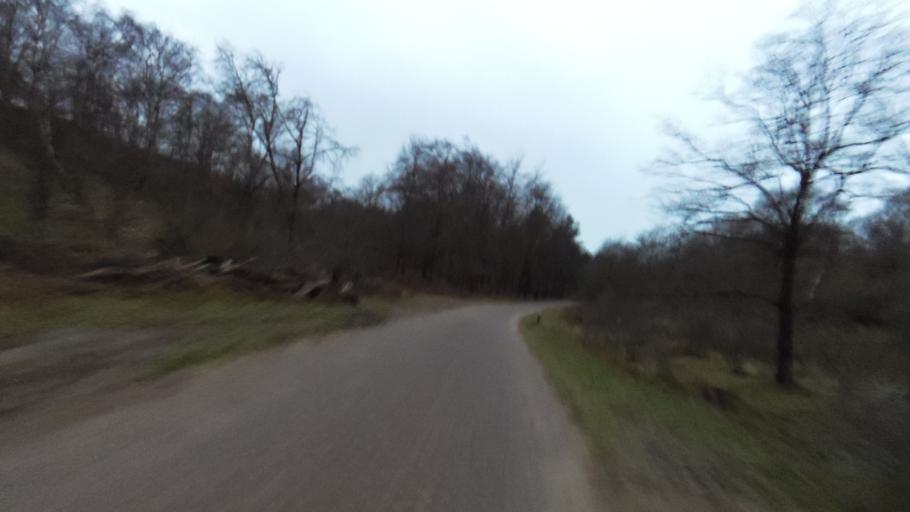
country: NL
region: North Holland
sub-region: Gemeente Beverwijk
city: Beverwijk
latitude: 52.5140
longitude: 4.6221
